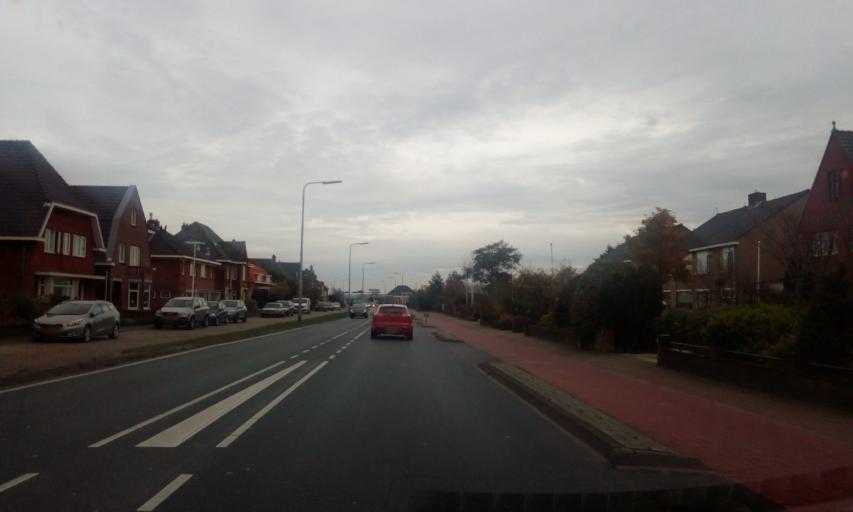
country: NL
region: South Holland
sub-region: Gemeente Westland
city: Monster
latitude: 52.0203
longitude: 4.1694
